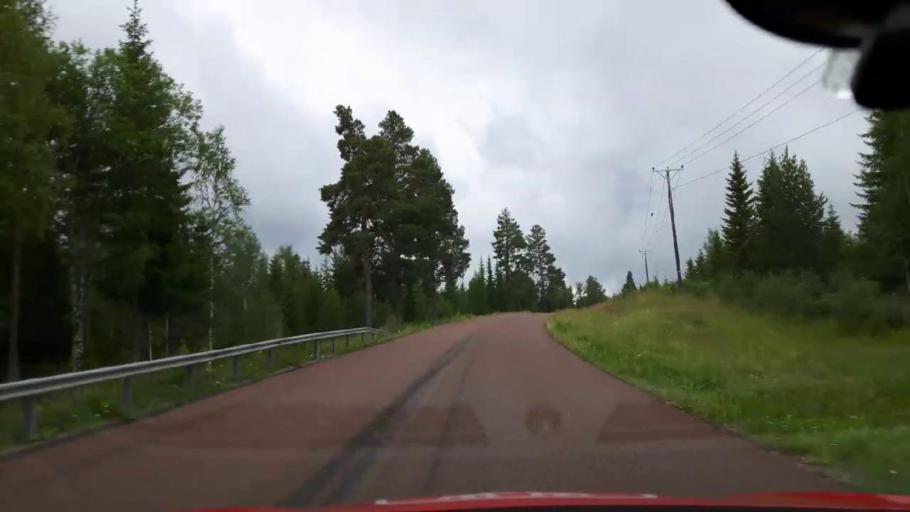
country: SE
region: Jaemtland
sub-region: Krokoms Kommun
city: Valla
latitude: 63.3455
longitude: 13.7226
